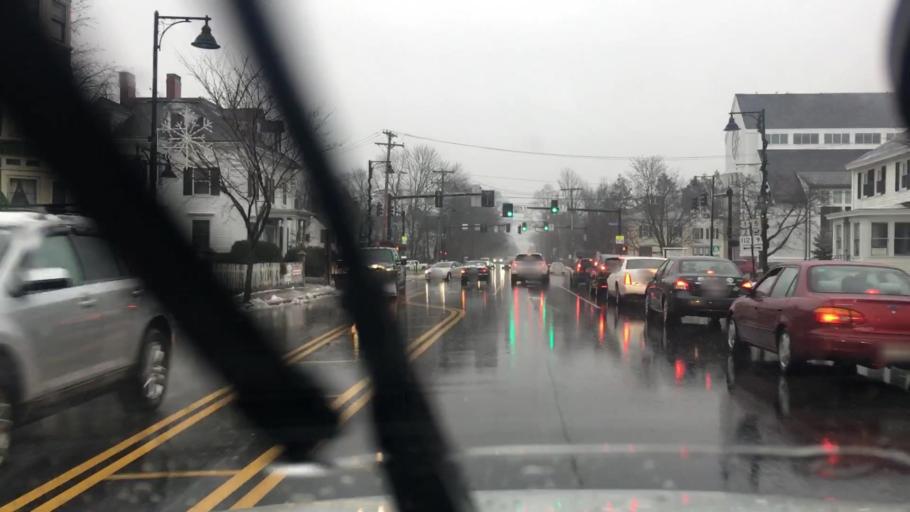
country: US
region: Maine
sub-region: York County
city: Saco
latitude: 43.5002
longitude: -70.4436
